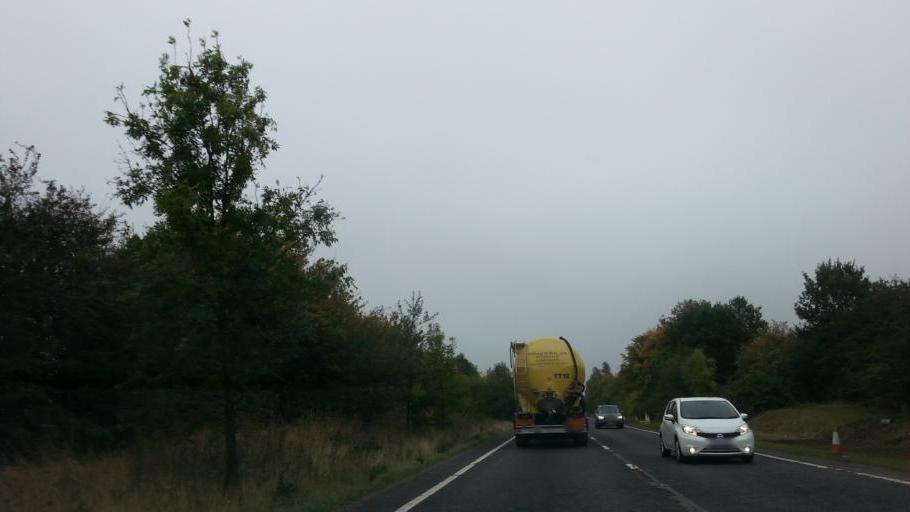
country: GB
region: England
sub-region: Northamptonshire
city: Thrapston
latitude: 52.3868
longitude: -0.5235
